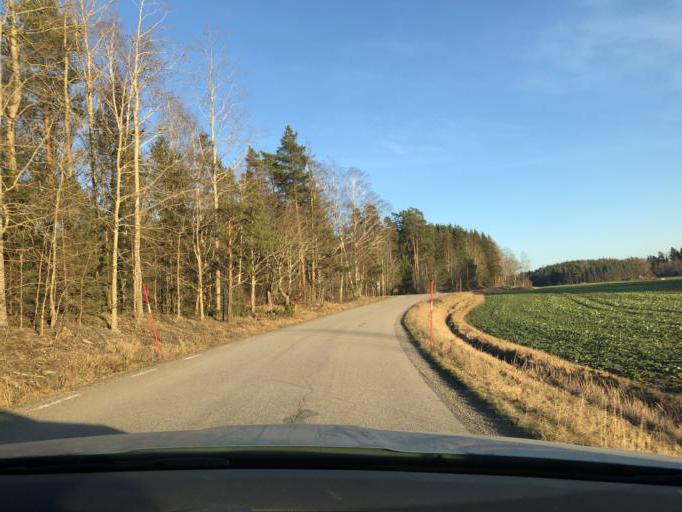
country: SE
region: Soedermanland
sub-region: Eskilstuna Kommun
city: Arla
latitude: 59.4196
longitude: 16.6607
